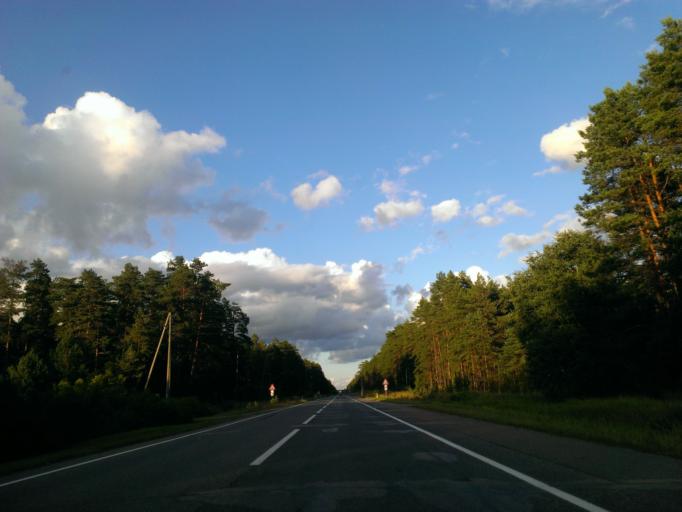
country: LV
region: Incukalns
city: Vangazi
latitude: 57.0754
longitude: 24.5101
